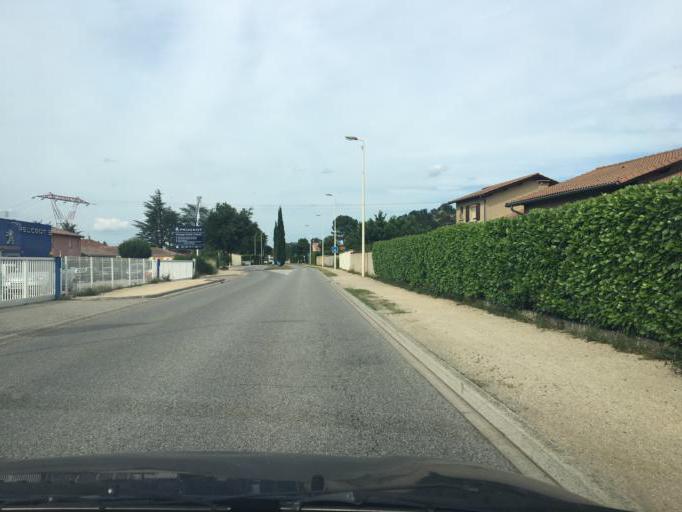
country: FR
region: Rhone-Alpes
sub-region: Departement de la Drome
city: Chateauneuf-sur-Isere
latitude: 45.0096
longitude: 4.9295
